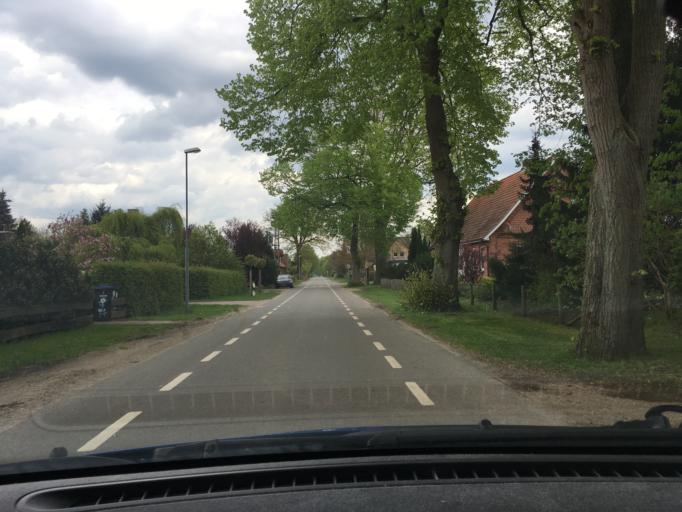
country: DE
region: Lower Saxony
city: Radbruch
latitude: 53.3038
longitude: 10.2744
